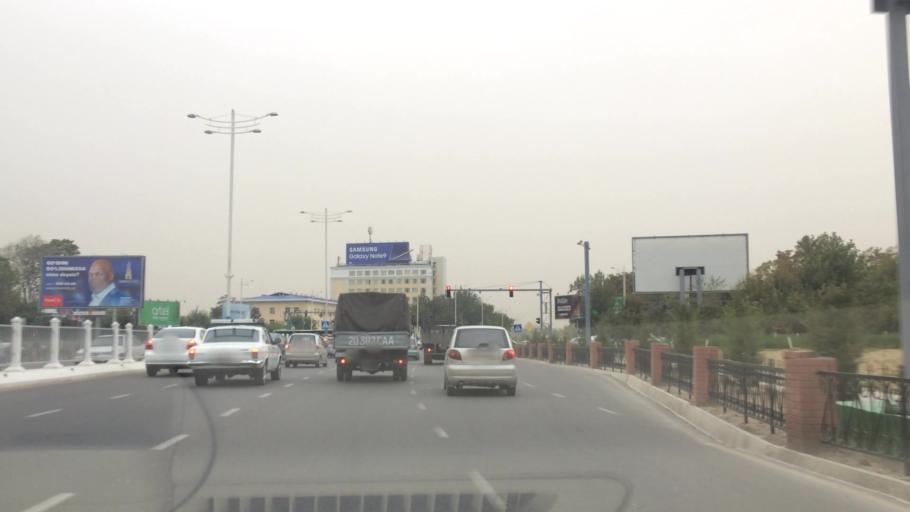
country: UZ
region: Toshkent Shahri
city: Bektemir
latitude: 41.3051
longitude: 69.3082
